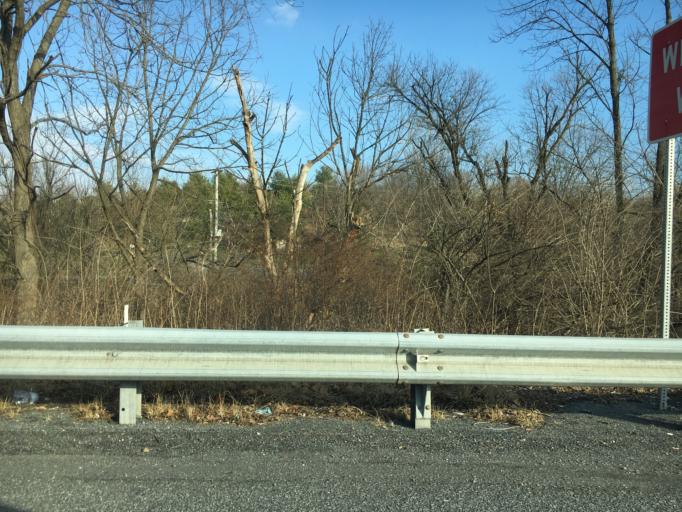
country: US
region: Pennsylvania
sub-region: Lehigh County
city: Stiles
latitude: 40.6725
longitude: -75.5163
